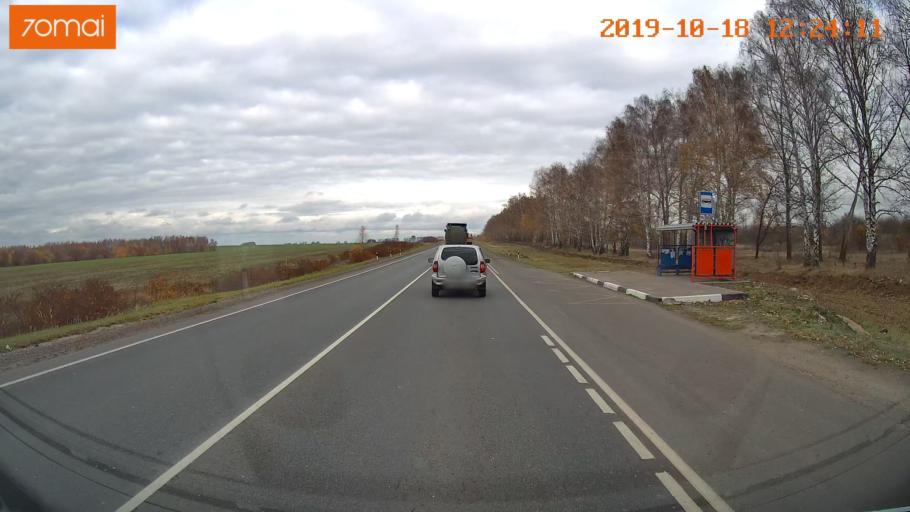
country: RU
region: Rjazan
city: Rybnoye
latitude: 54.5370
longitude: 39.5122
